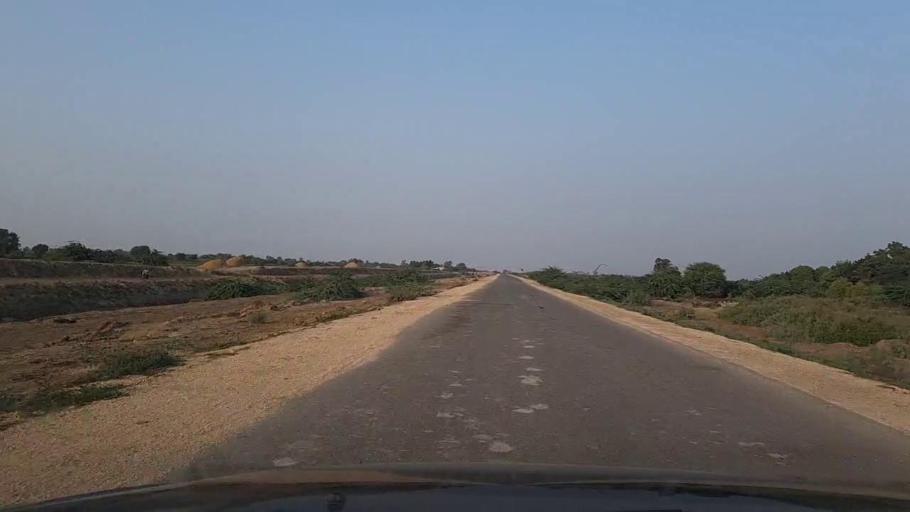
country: PK
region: Sindh
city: Mirpur Sakro
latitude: 24.4810
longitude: 67.8050
